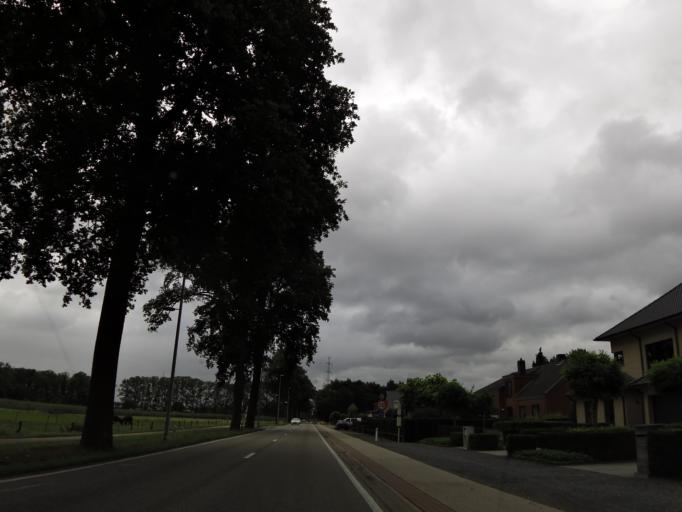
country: BE
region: Flanders
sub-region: Provincie Limburg
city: Kinrooi
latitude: 51.0994
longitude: 5.7375
